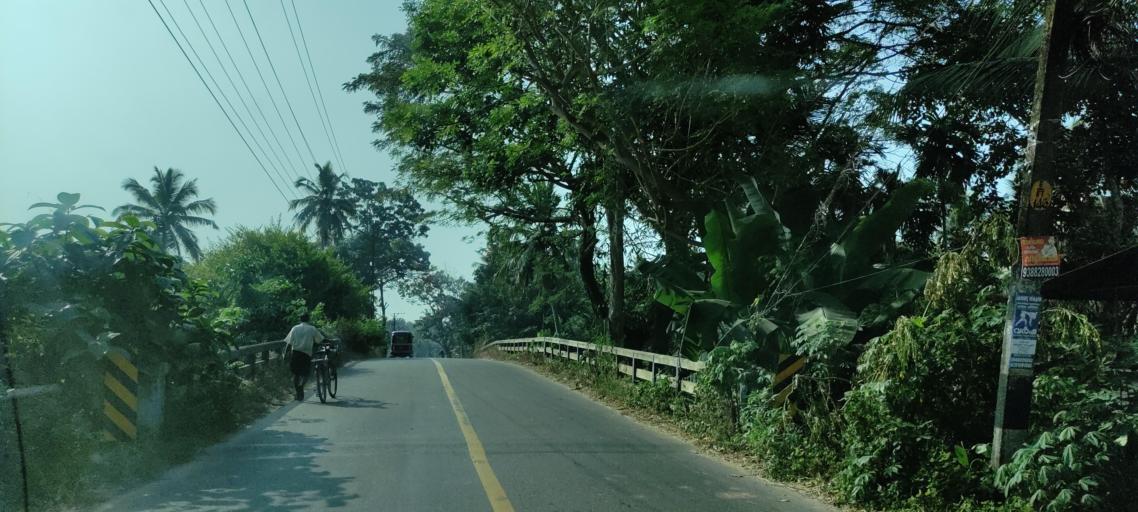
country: IN
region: Kerala
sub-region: Kottayam
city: Changanacheri
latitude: 9.3629
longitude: 76.4492
